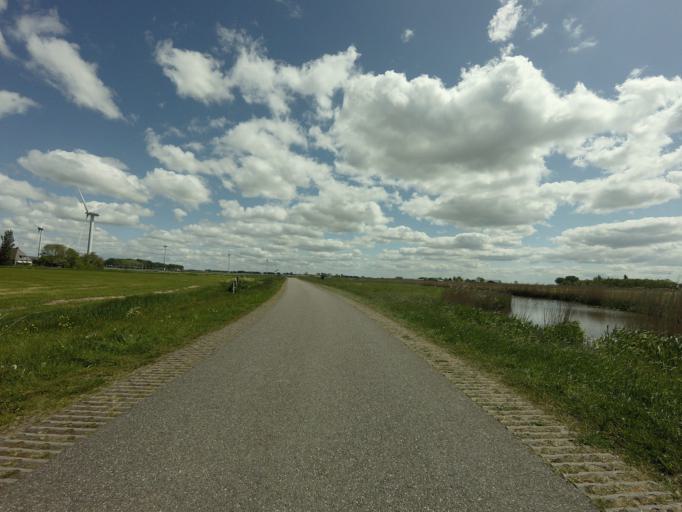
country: NL
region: Friesland
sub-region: Sudwest Fryslan
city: Makkum
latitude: 53.0892
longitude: 5.4188
